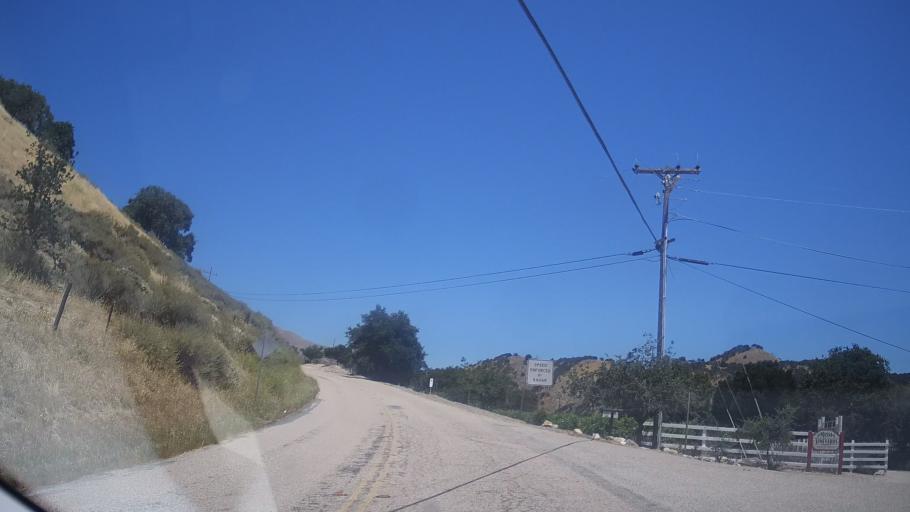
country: US
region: California
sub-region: Monterey County
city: Greenfield
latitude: 36.2574
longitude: -121.4221
